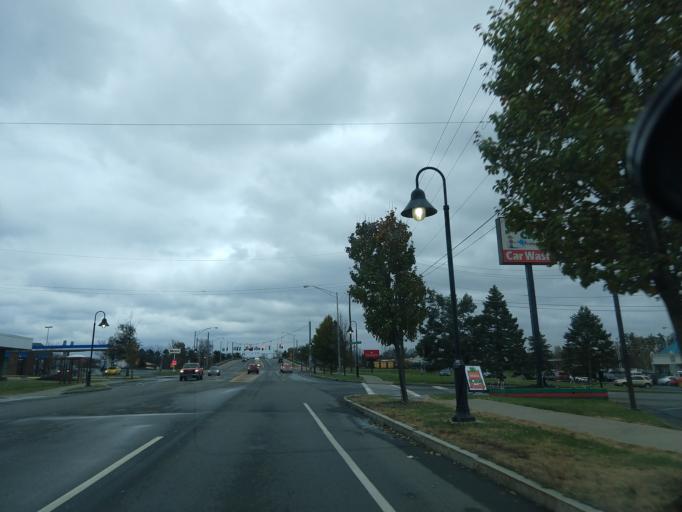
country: US
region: New York
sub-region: Tompkins County
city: Lansing
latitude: 42.4840
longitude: -76.4859
